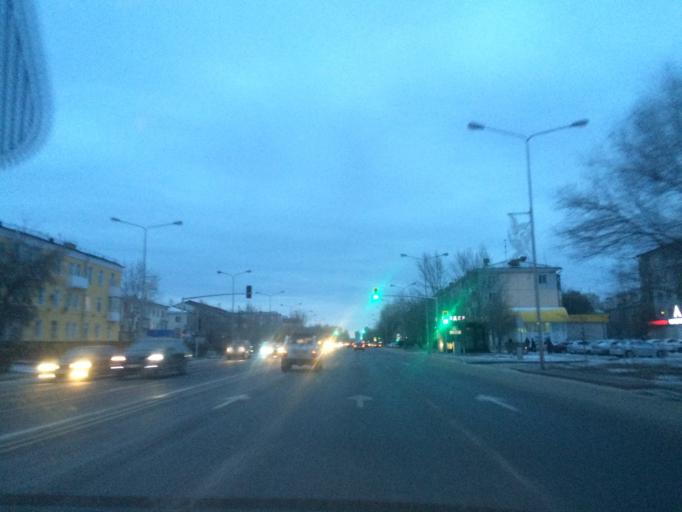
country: KZ
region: Astana Qalasy
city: Astana
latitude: 51.1840
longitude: 71.4087
